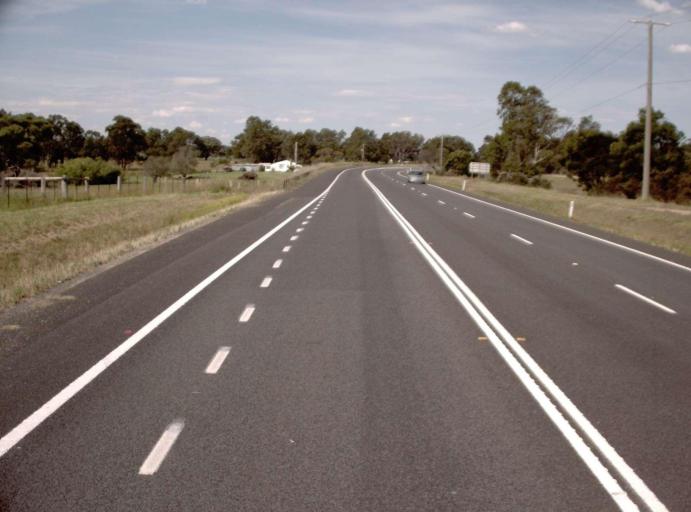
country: AU
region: Victoria
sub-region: East Gippsland
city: Lakes Entrance
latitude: -37.8199
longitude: 147.8109
